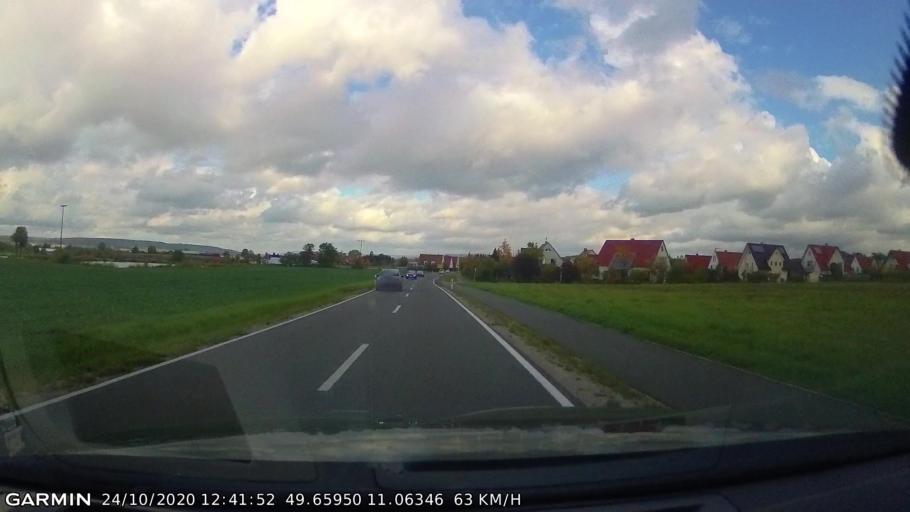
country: DE
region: Bavaria
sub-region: Upper Franconia
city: Poxdorf
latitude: 49.6595
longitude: 11.0634
